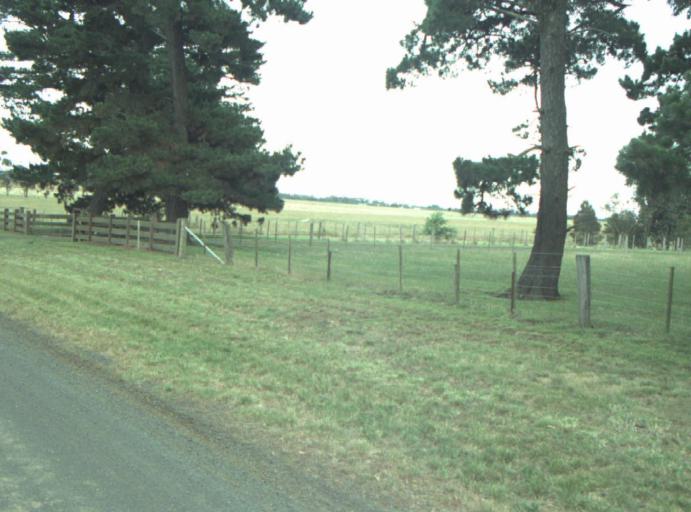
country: AU
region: Victoria
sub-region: Greater Geelong
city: Clifton Springs
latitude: -38.1914
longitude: 144.5992
